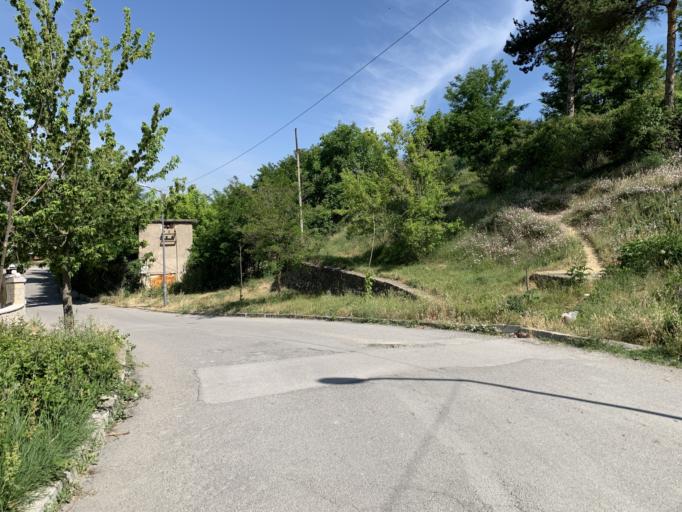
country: AL
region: Korce
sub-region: Rrethi i Korces
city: Korce
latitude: 40.6175
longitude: 20.7880
